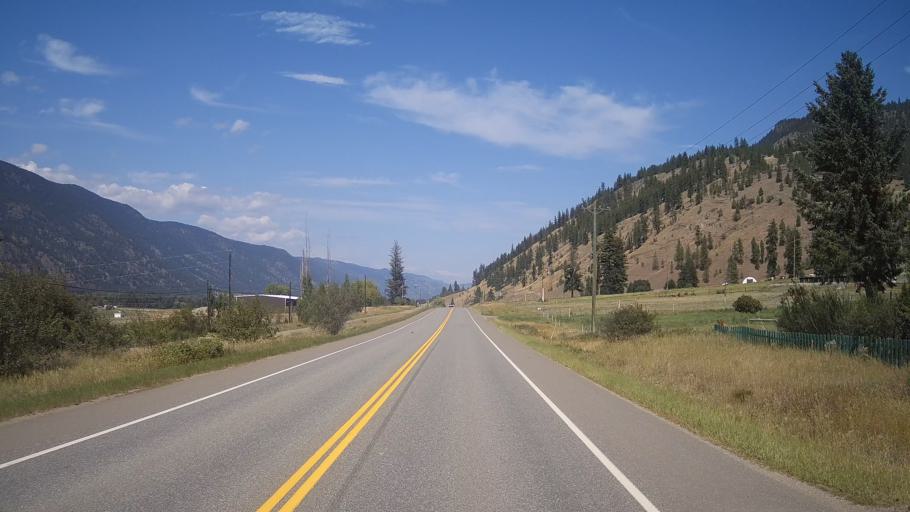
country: CA
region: British Columbia
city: Kamloops
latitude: 50.9265
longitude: -120.2358
